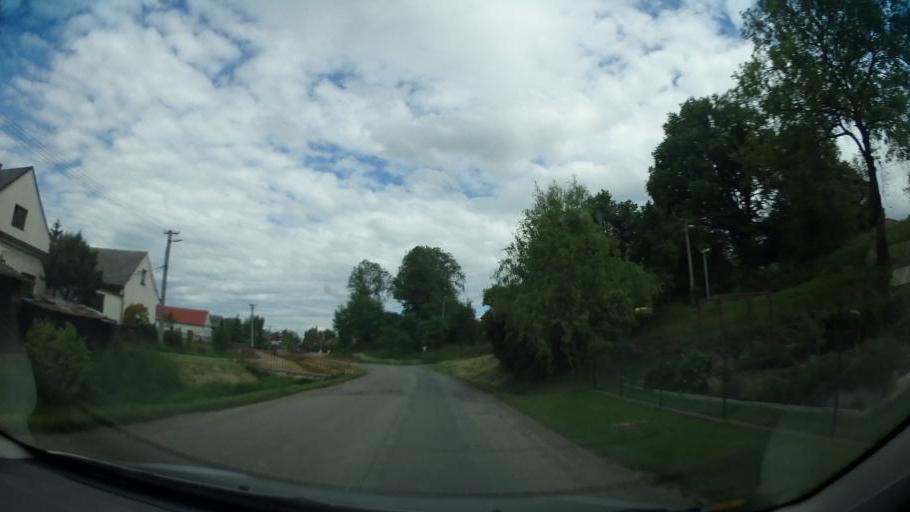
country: CZ
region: Pardubicky
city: Kuncina
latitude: 49.8379
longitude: 16.6994
